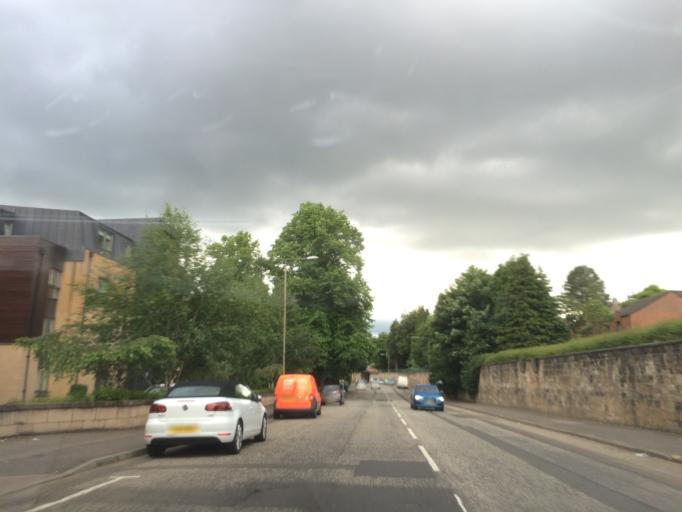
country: GB
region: Scotland
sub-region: East Renfrewshire
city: Giffnock
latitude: 55.8255
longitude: -4.2737
